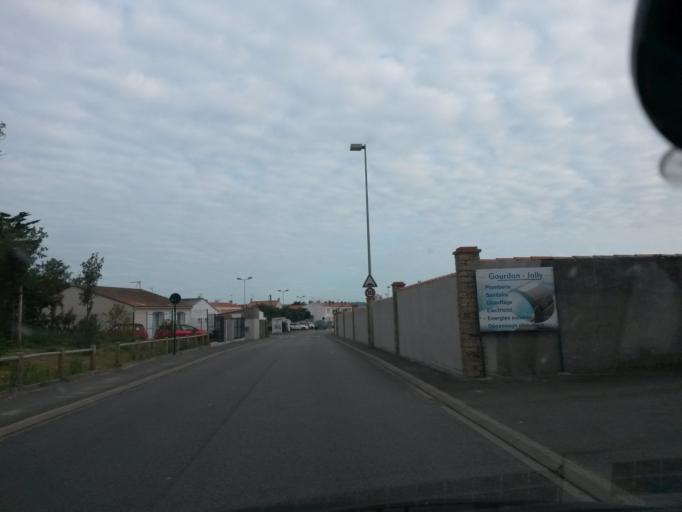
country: FR
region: Pays de la Loire
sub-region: Departement de la Vendee
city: Les Sables-d'Olonne
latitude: 46.5003
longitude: -1.8037
